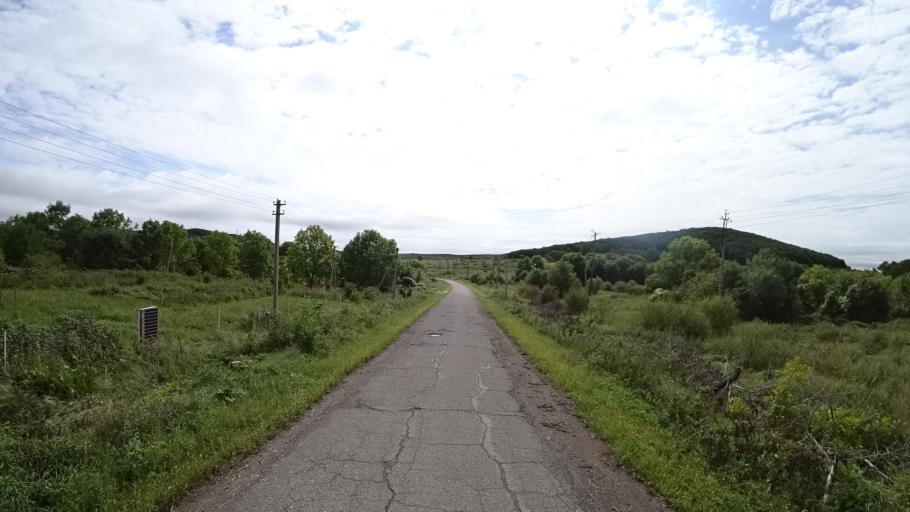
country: RU
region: Primorskiy
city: Lyalichi
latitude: 44.1372
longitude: 132.3877
